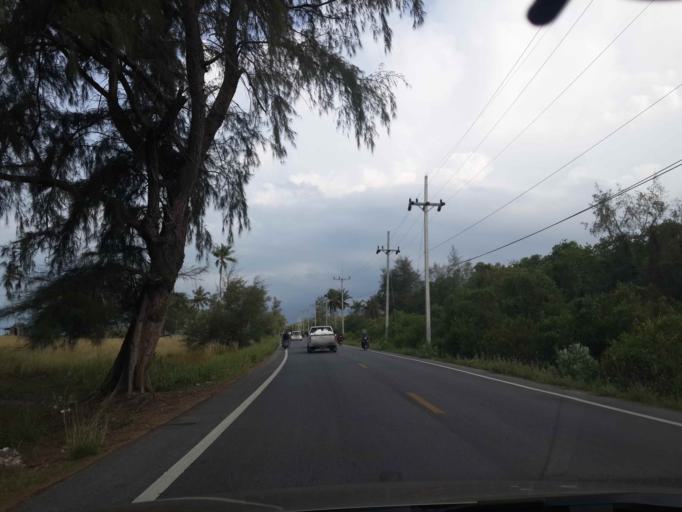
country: TH
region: Pattani
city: Yaring
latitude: 6.9088
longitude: 101.3472
